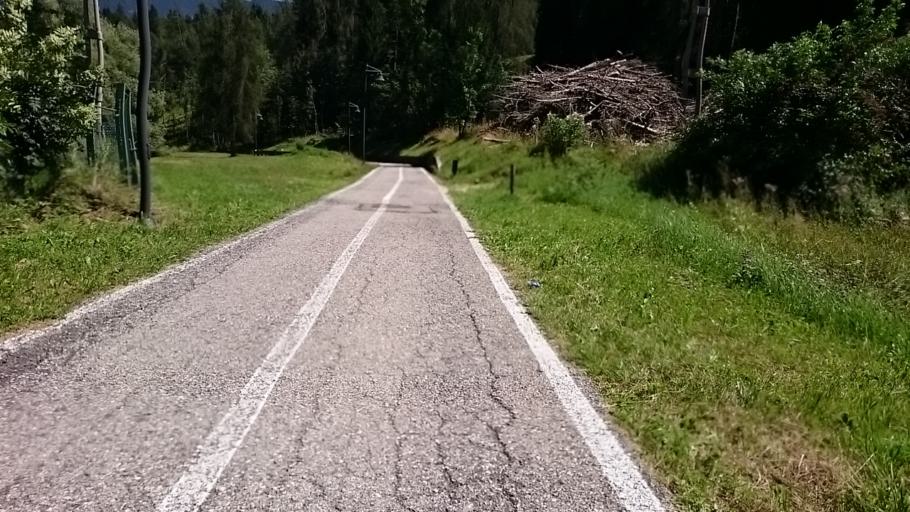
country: IT
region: Veneto
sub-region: Provincia di Belluno
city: Pieve di Cadore
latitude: 46.4197
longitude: 12.3517
